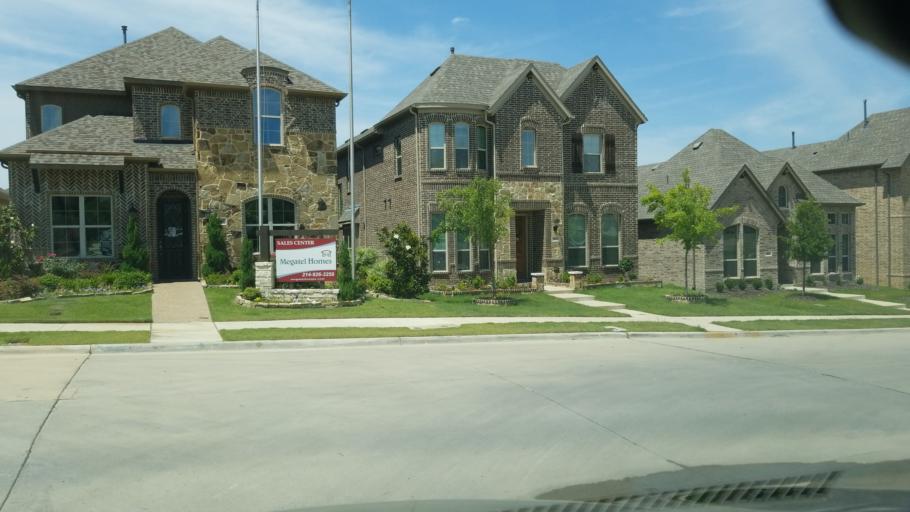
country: US
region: Texas
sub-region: Dallas County
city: Coppell
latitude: 32.8783
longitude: -96.9962
